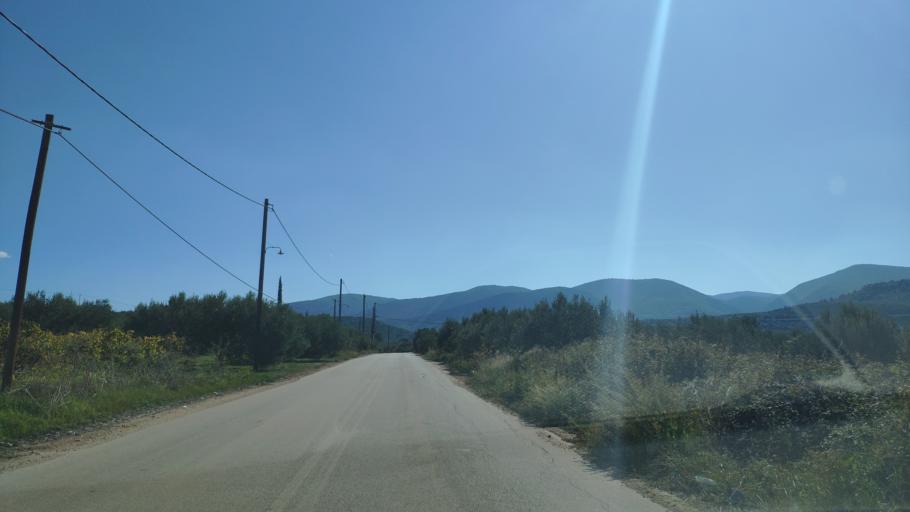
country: GR
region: Peloponnese
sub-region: Nomos Korinthias
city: Athikia
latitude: 37.8426
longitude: 22.9064
